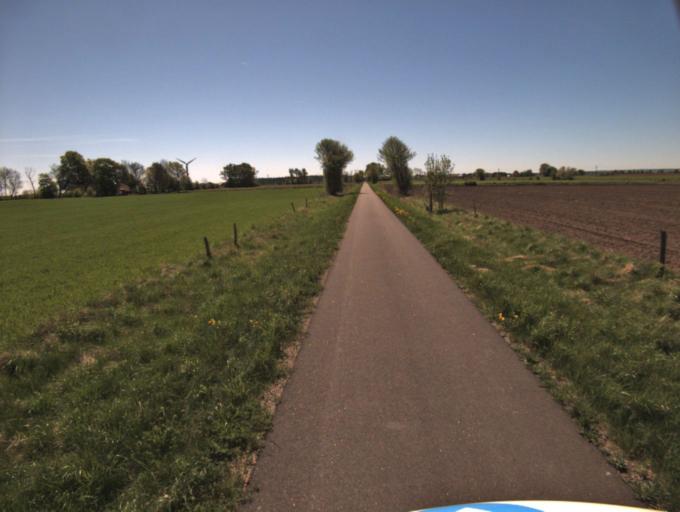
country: SE
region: Skane
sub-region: Kristianstads Kommun
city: Norra Asum
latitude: 55.9668
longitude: 14.1580
